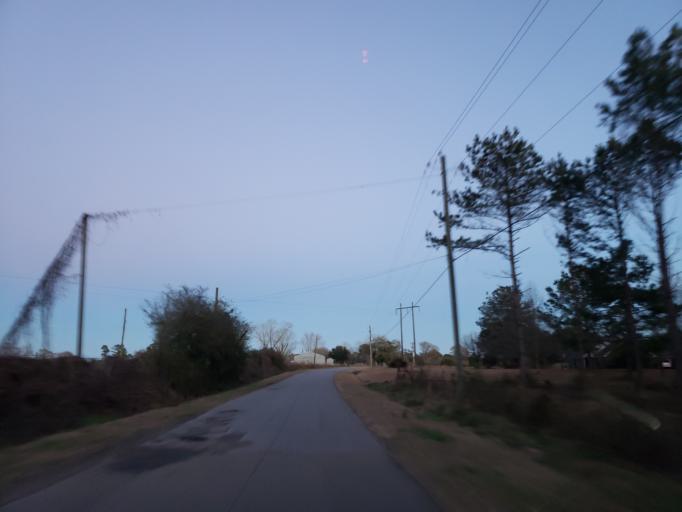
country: US
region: Mississippi
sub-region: Forrest County
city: Rawls Springs
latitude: 31.4387
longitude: -89.3746
